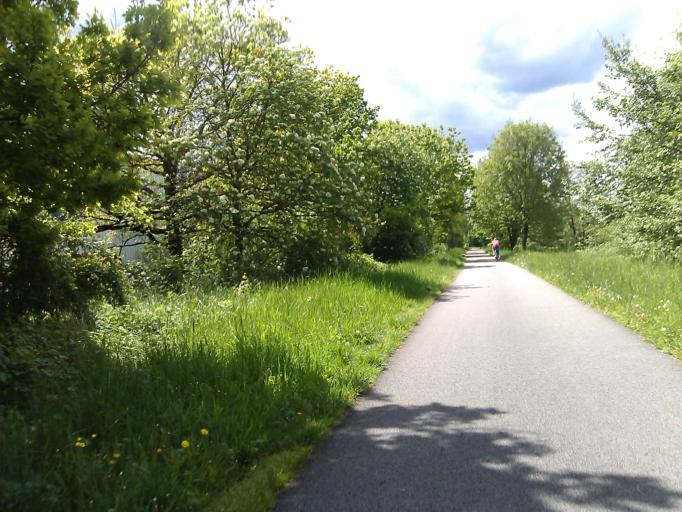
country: FR
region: Franche-Comte
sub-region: Departement du Doubs
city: Sochaux
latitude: 47.5040
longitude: 6.8311
